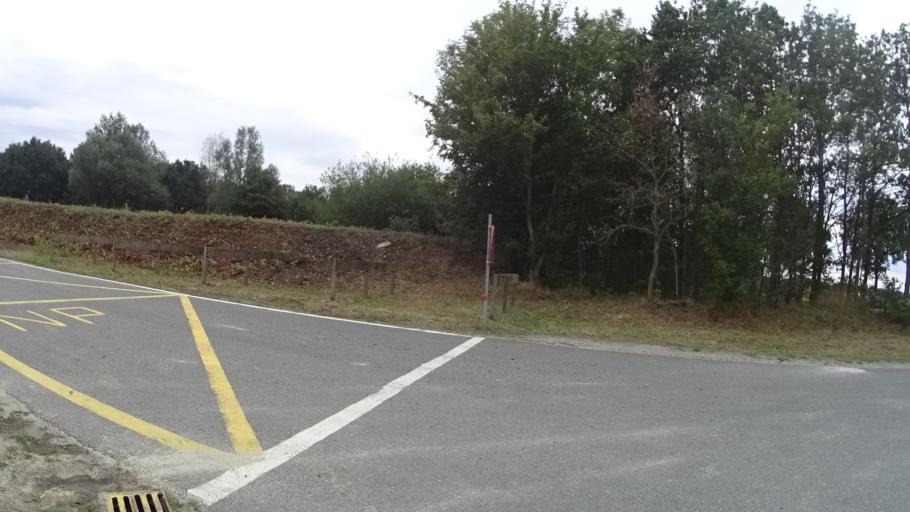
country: NL
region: Groningen
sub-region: Gemeente Slochteren
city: Slochteren
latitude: 53.1804
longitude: 6.8508
